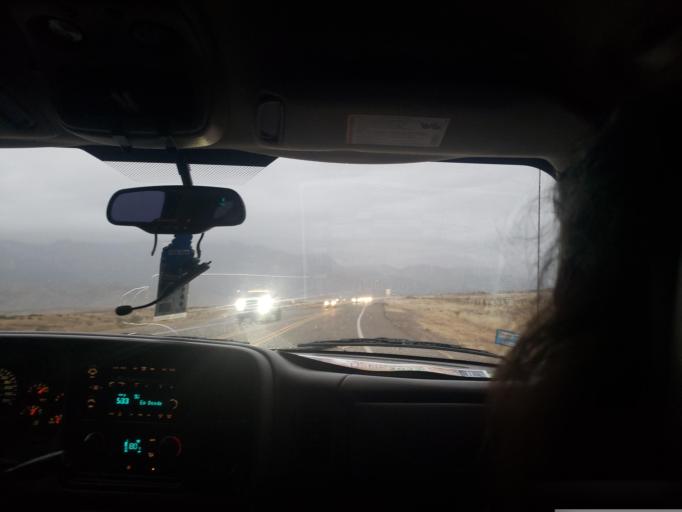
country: US
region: New Mexico
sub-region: Sandoval County
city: Corrales
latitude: 35.2024
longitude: -106.5554
